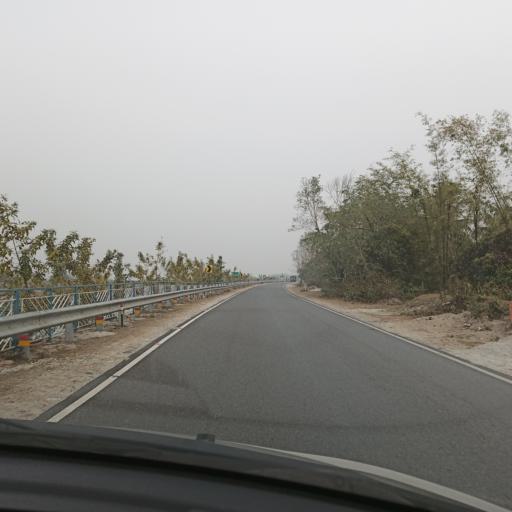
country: IN
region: West Bengal
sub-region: Jalpaiguri
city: Odlabari
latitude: 26.7369
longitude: 88.5752
